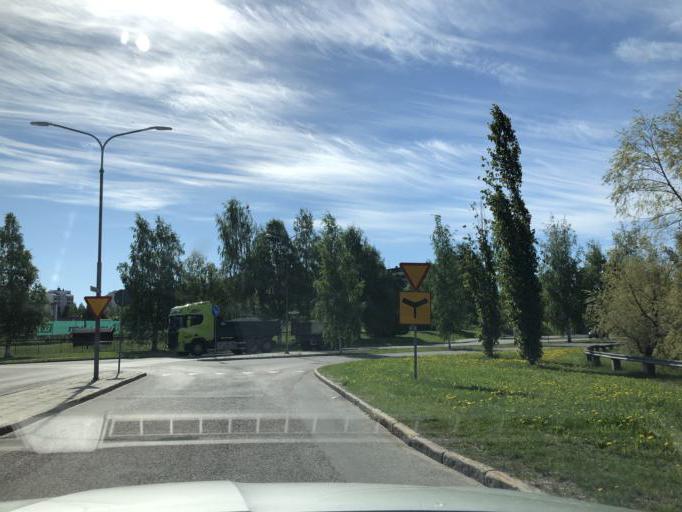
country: SE
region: Norrbotten
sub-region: Pitea Kommun
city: Pitea
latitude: 65.3152
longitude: 21.4912
